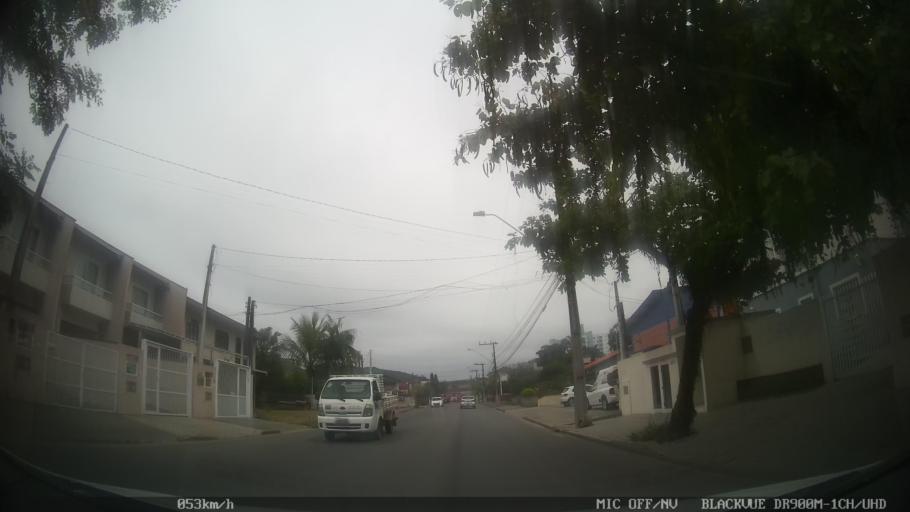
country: BR
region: Santa Catarina
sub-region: Joinville
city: Joinville
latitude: -26.2689
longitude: -48.8203
